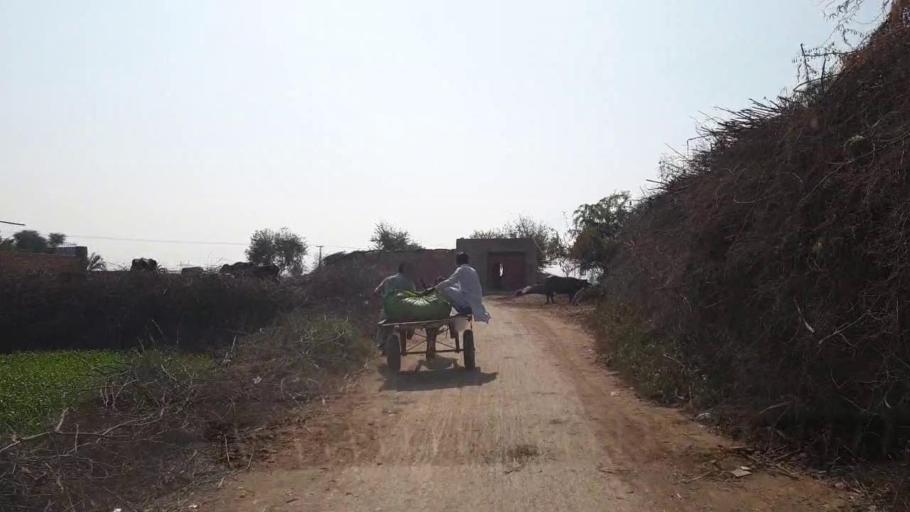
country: PK
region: Sindh
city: Hala
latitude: 25.9102
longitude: 68.4536
